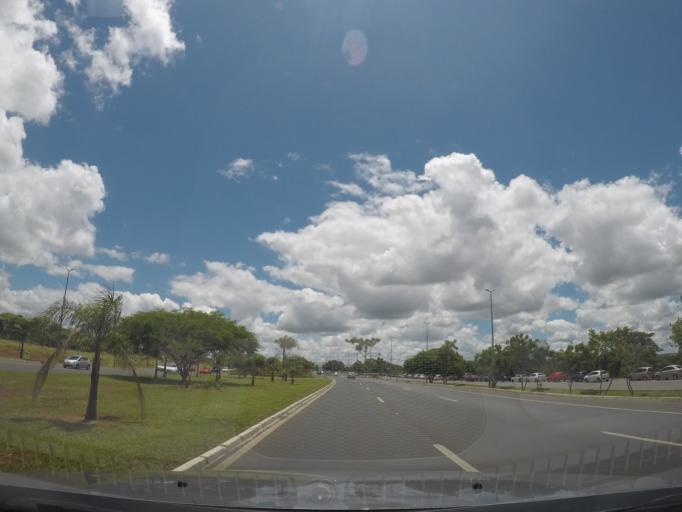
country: BR
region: Federal District
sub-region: Brasilia
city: Brasilia
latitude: -15.8430
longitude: -47.9457
